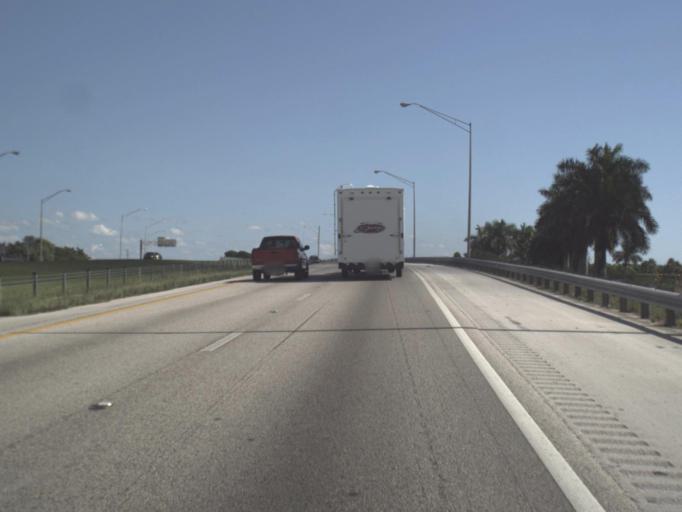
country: US
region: Florida
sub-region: Miami-Dade County
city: Goulds
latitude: 25.5317
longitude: -80.3745
